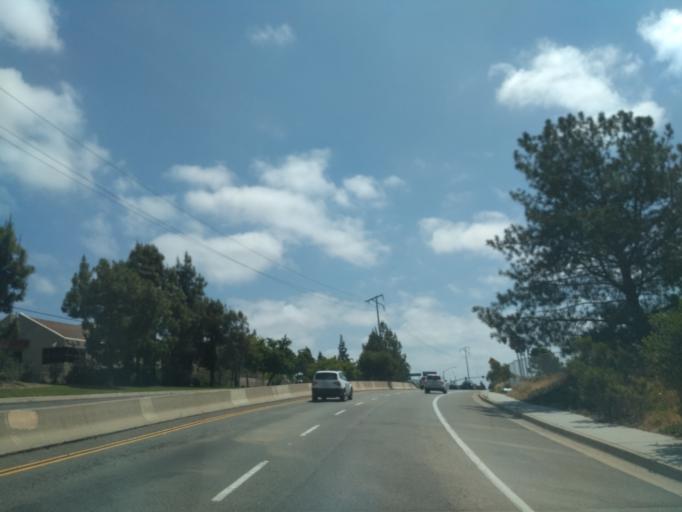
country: US
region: California
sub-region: San Diego County
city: La Jolla
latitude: 32.8115
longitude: -117.2036
